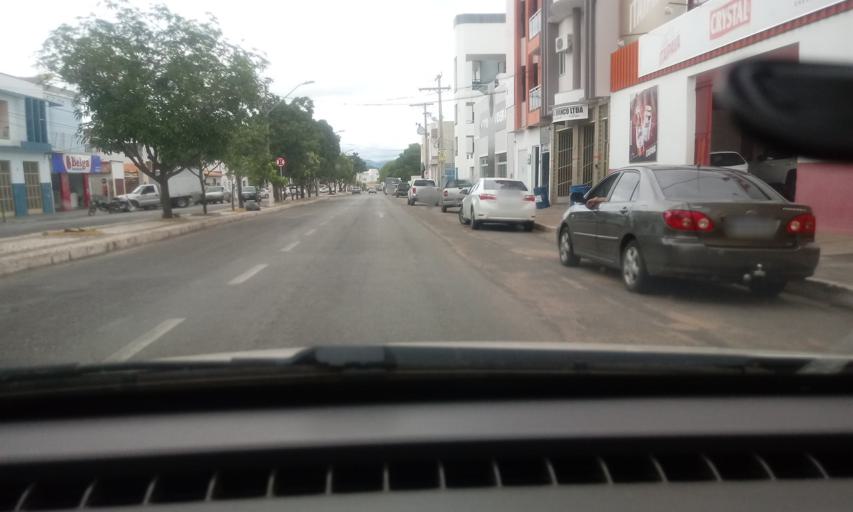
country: BR
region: Bahia
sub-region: Guanambi
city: Guanambi
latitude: -14.2173
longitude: -42.7826
